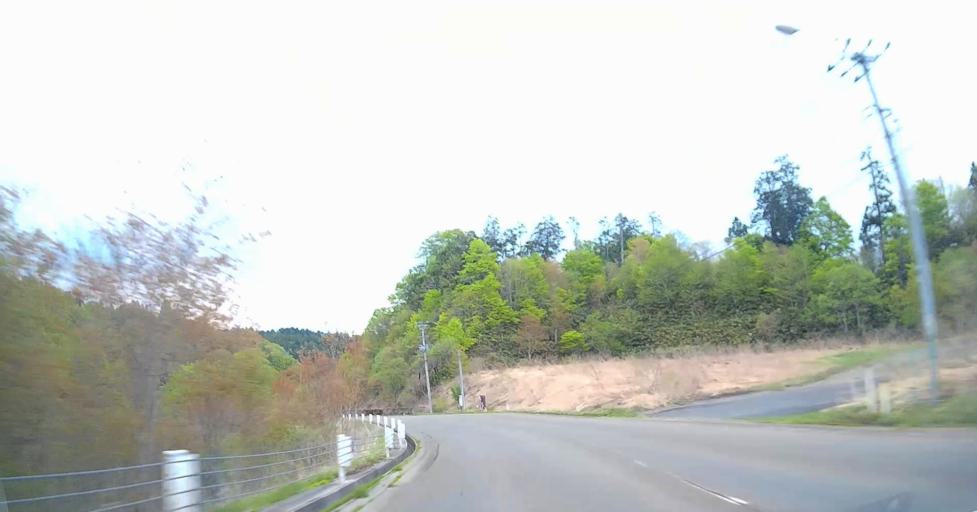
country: JP
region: Aomori
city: Goshogawara
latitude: 41.1018
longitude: 140.5485
